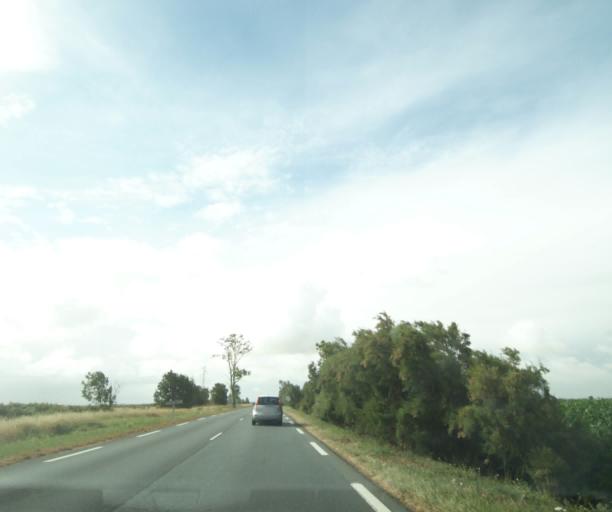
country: FR
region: Poitou-Charentes
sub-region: Departement de la Charente-Maritime
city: Charron
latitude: 46.2898
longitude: -1.0831
